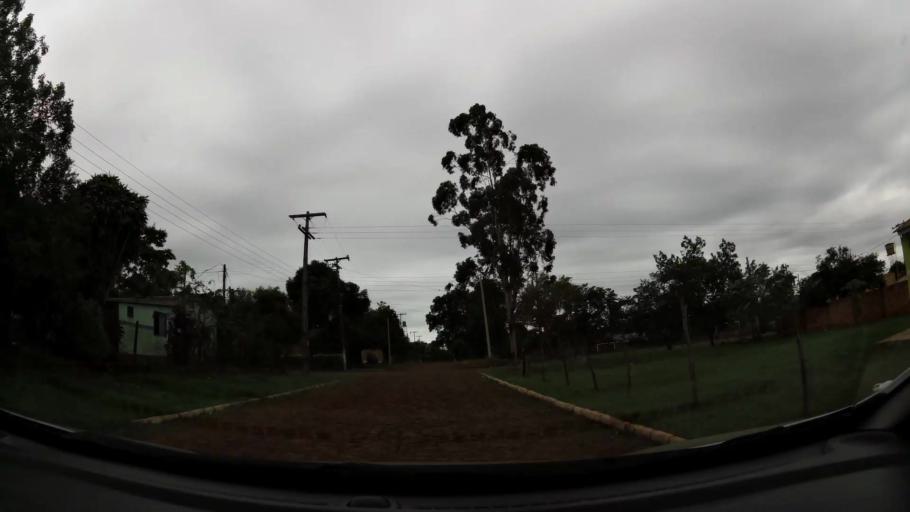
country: PY
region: Alto Parana
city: Ciudad del Este
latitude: -25.4391
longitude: -54.6407
